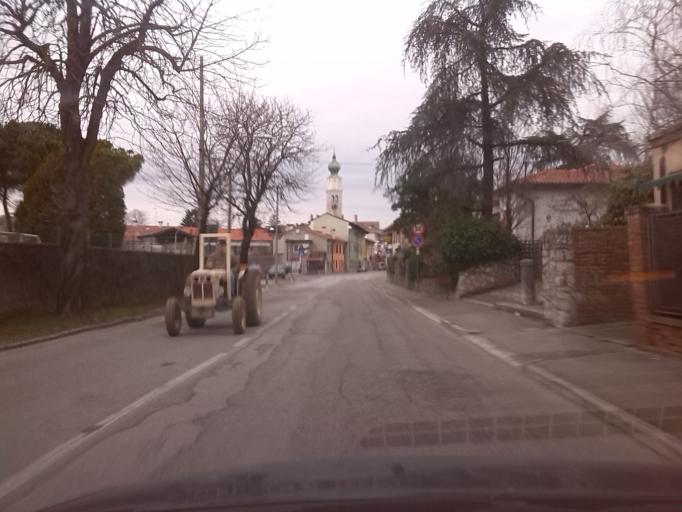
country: IT
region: Friuli Venezia Giulia
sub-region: Provincia di Gorizia
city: Romans d'Isonzo
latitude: 45.8881
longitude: 13.4401
